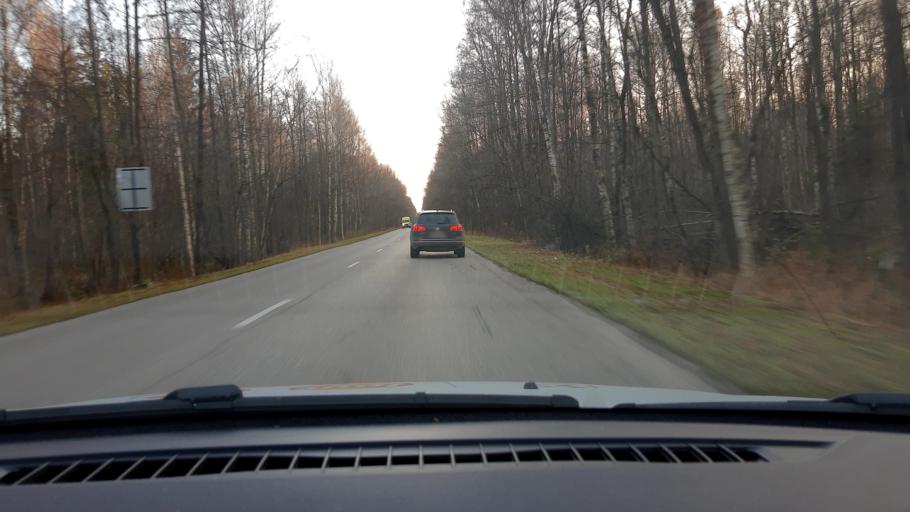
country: RU
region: Nizjnij Novgorod
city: Volodarsk
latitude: 56.2761
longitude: 43.1666
